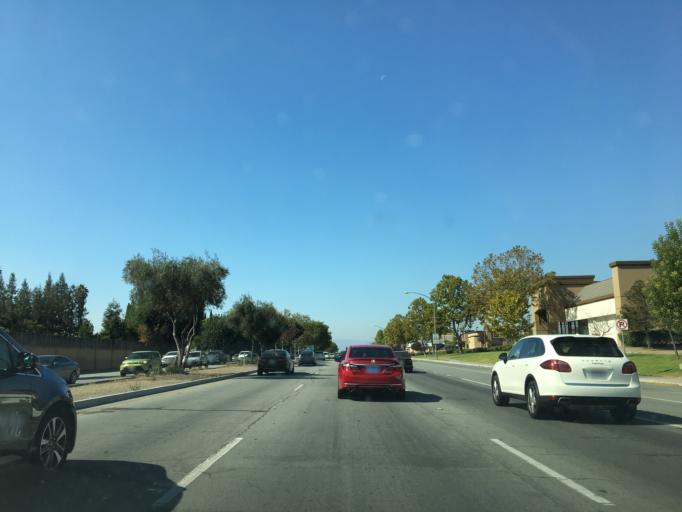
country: US
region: California
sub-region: Santa Clara County
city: Seven Trees
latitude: 37.2747
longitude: -121.8505
